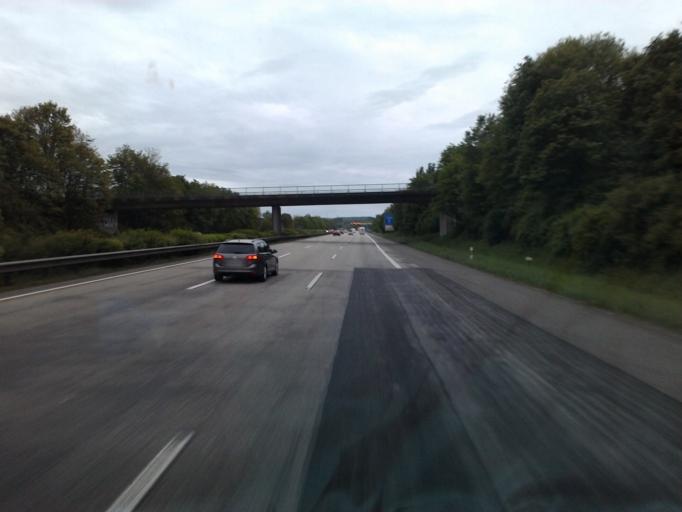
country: DE
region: Rheinland-Pfalz
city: Niederzissen
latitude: 50.4506
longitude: 7.2303
